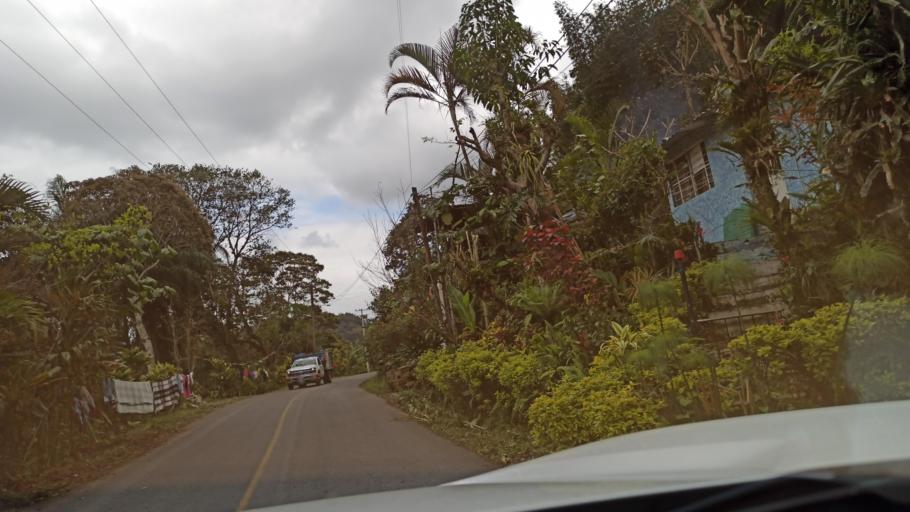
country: MX
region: Veracruz
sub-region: Fortin
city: Fortin de las Flores
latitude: 18.8915
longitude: -97.0050
